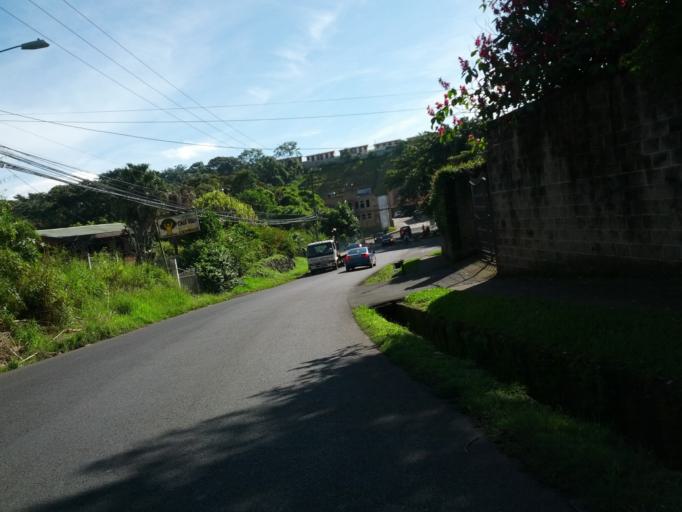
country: CR
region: Alajuela
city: Alajuela
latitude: 10.0194
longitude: -84.1989
